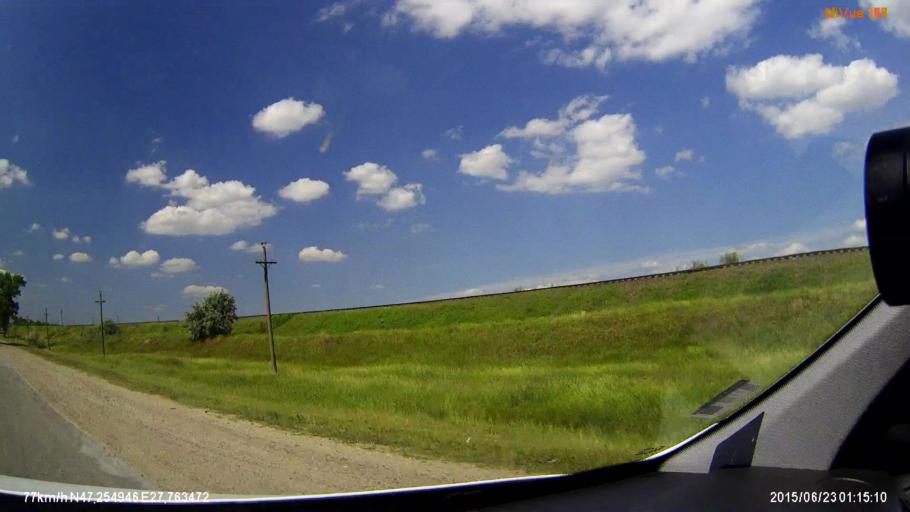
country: RO
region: Iasi
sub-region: Comuna Ungheni
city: Bosia
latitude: 47.2548
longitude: 27.7636
